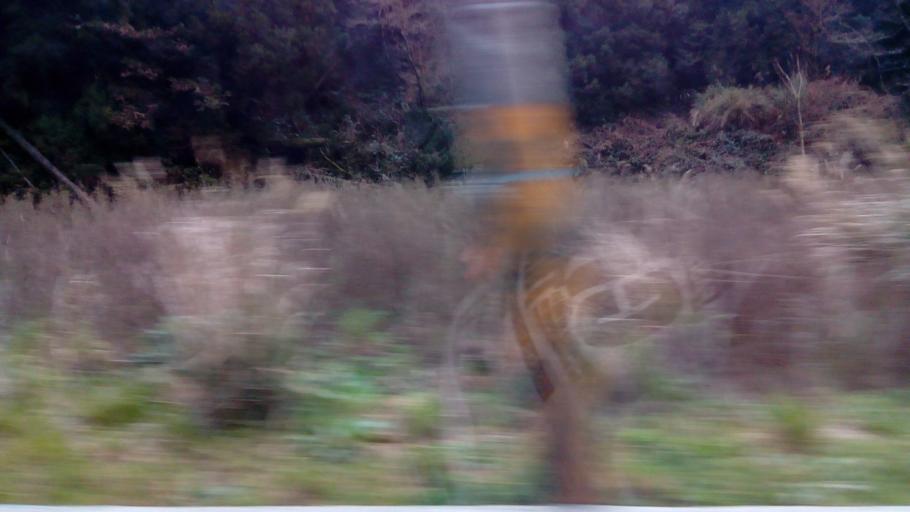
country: TW
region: Taiwan
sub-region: Hualien
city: Hualian
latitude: 24.3948
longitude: 121.3543
